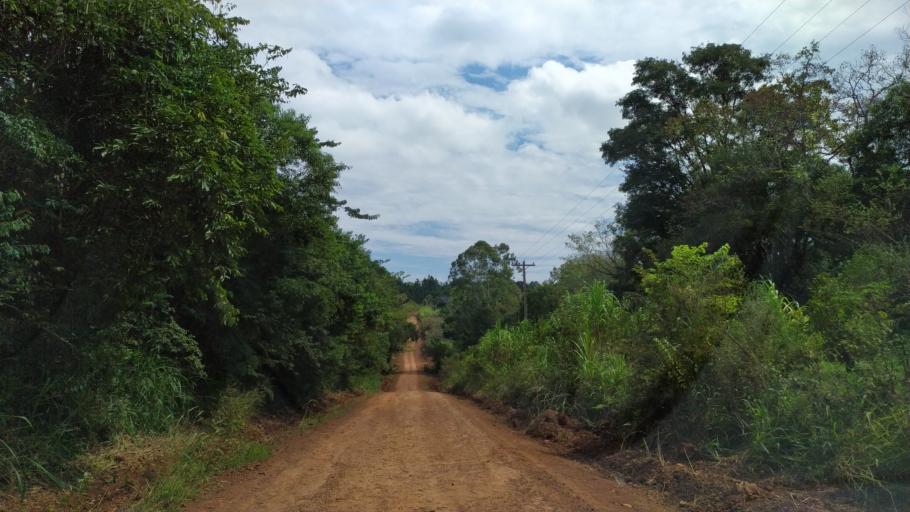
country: AR
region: Misiones
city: Puerto Piray
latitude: -26.5353
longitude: -54.6412
